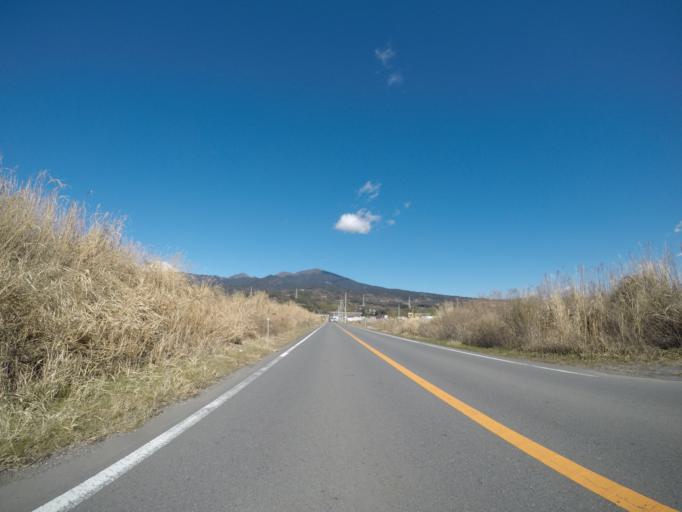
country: JP
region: Shizuoka
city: Numazu
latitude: 35.1398
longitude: 138.7847
